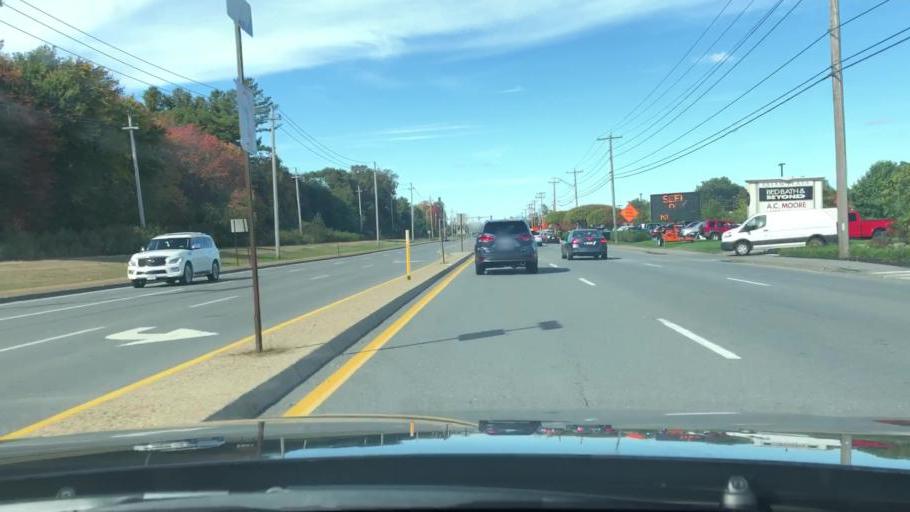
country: US
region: New Hampshire
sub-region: Rockingham County
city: Salem
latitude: 42.7609
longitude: -71.2141
